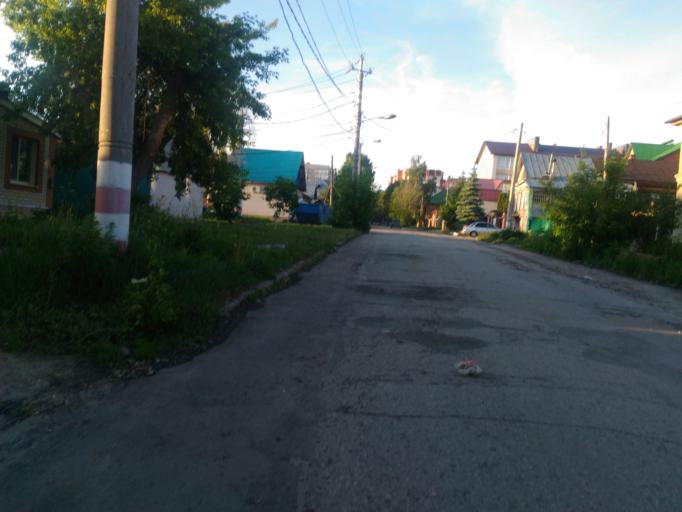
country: RU
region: Ulyanovsk
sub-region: Ulyanovskiy Rayon
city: Ulyanovsk
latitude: 54.3183
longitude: 48.3792
